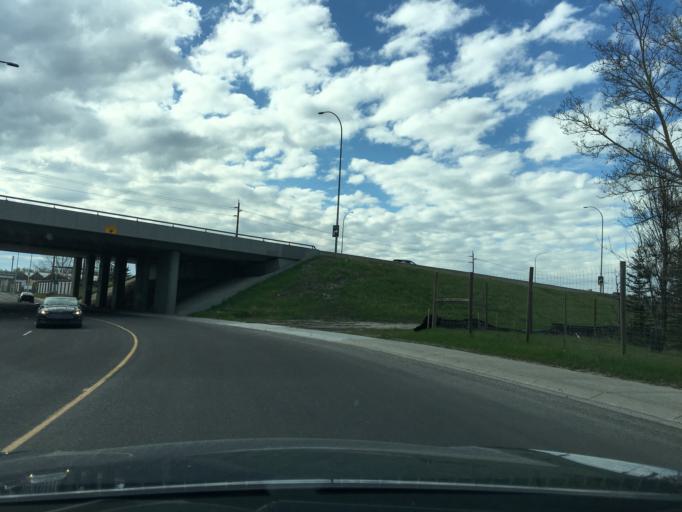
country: CA
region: Alberta
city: Calgary
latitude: 50.9259
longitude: -114.0703
